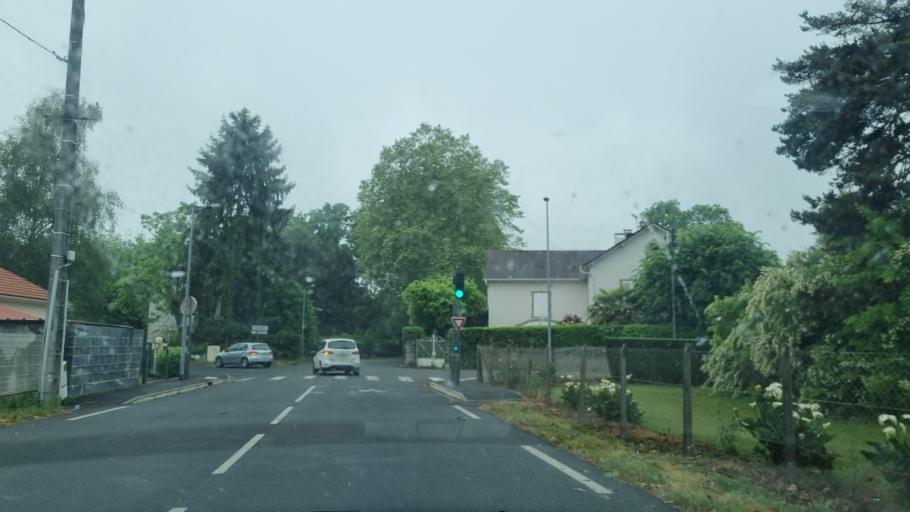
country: FR
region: Aquitaine
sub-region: Departement des Pyrenees-Atlantiques
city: Pau
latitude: 43.3265
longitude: -0.3412
